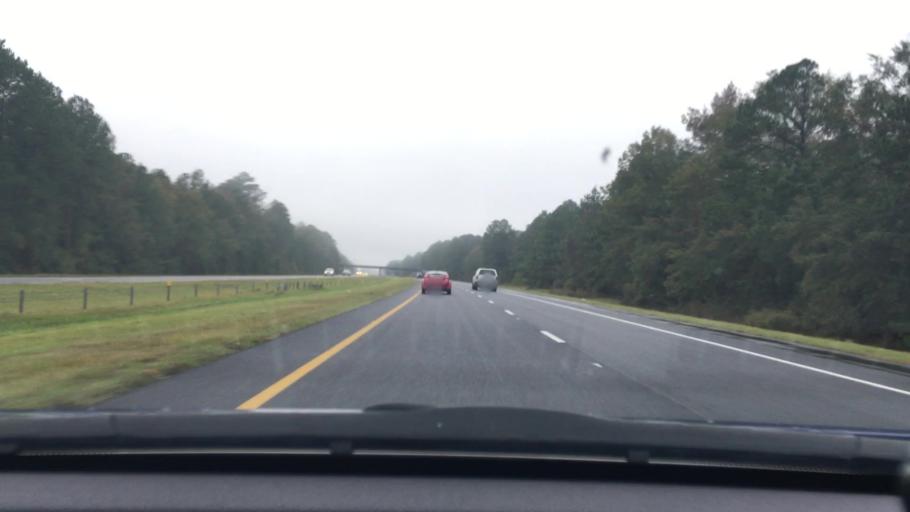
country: US
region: South Carolina
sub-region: Lee County
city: Bishopville
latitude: 34.1985
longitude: -80.0919
